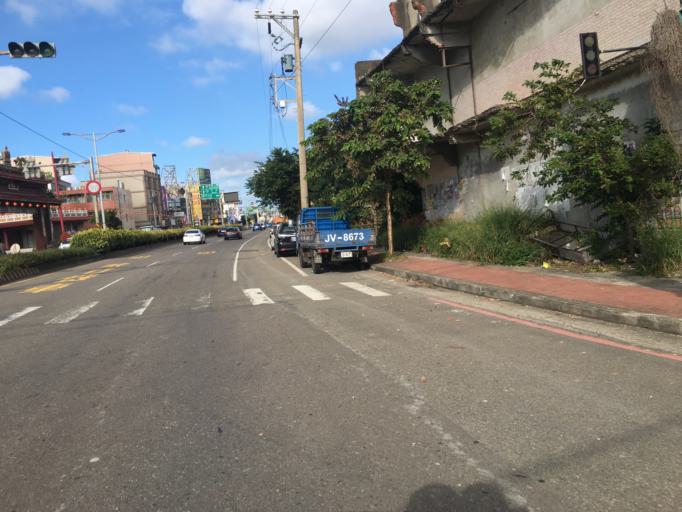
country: TW
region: Taiwan
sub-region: Hsinchu
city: Hsinchu
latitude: 24.8380
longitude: 120.9304
